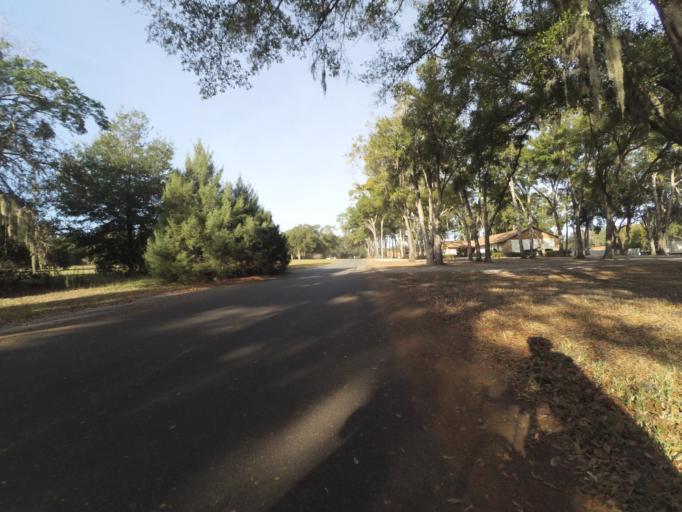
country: US
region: Florida
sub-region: Lake County
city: Umatilla
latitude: 28.9632
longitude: -81.6466
